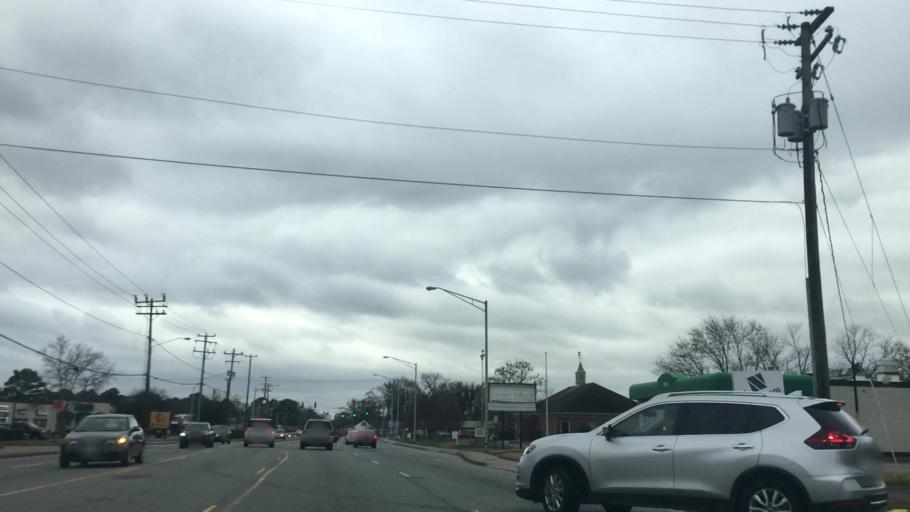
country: US
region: Virginia
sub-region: City of Chesapeake
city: Chesapeake
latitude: 36.8562
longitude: -76.1772
